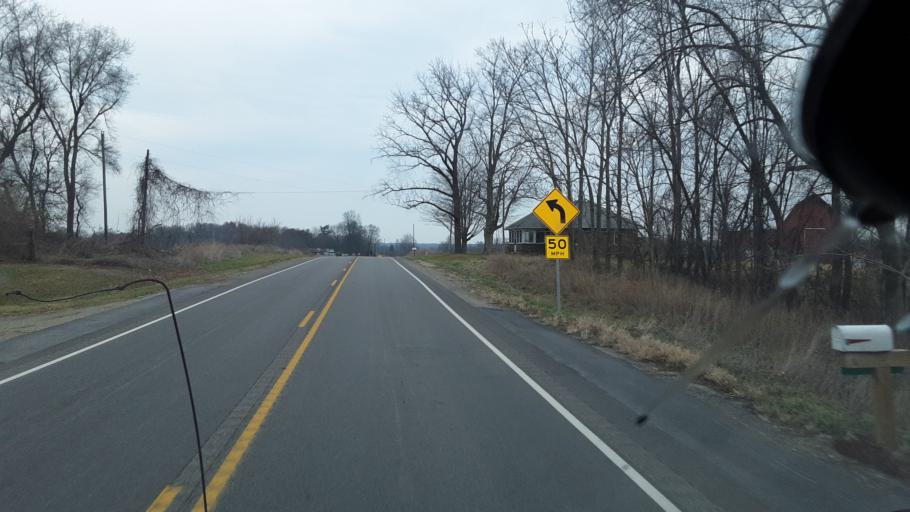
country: US
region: Indiana
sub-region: Steuben County
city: Angola
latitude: 41.6226
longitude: -85.1699
